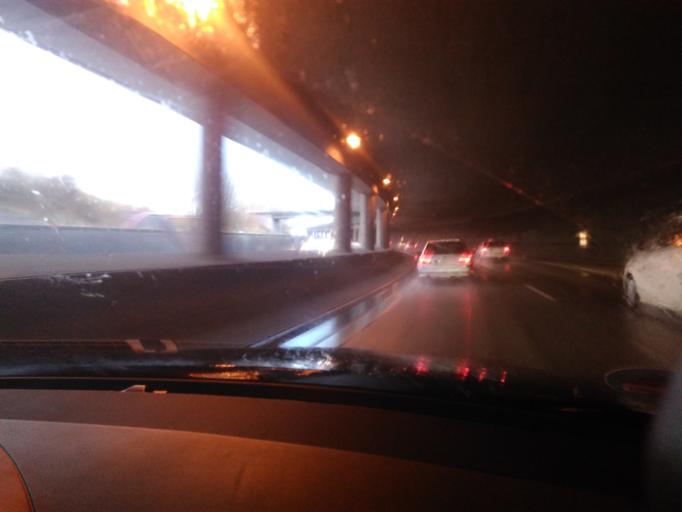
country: DE
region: Hamburg
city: Fuhlsbuettel
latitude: 53.6403
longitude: 10.0045
